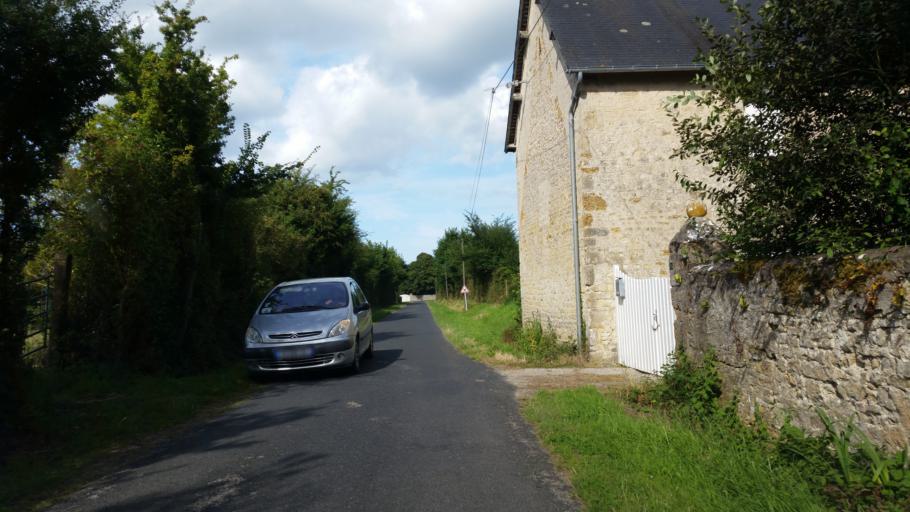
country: FR
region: Lower Normandy
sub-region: Departement de la Manche
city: Sainte-Mere-Eglise
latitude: 49.4490
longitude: -1.2560
